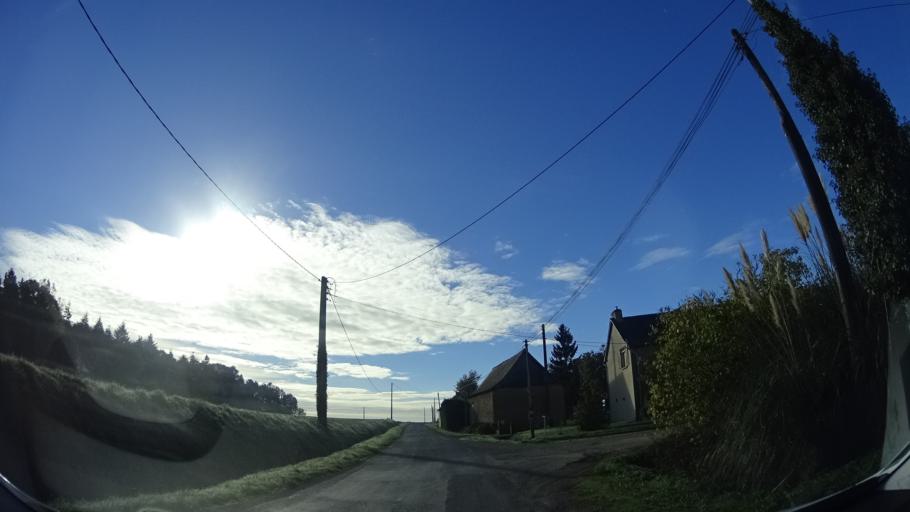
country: FR
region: Brittany
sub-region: Departement d'Ille-et-Vilaine
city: Geveze
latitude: 48.2082
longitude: -1.7745
